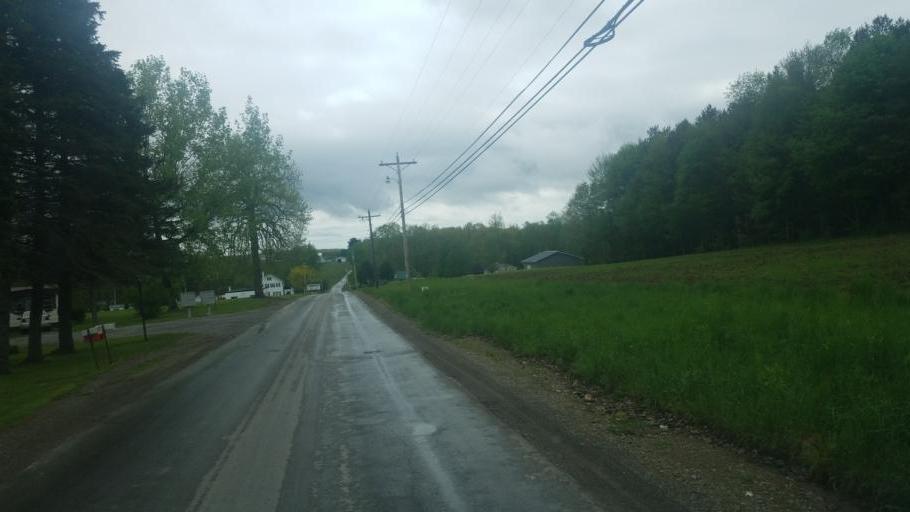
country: US
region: Pennsylvania
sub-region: Forest County
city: Tionesta
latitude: 41.3921
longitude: -79.3881
